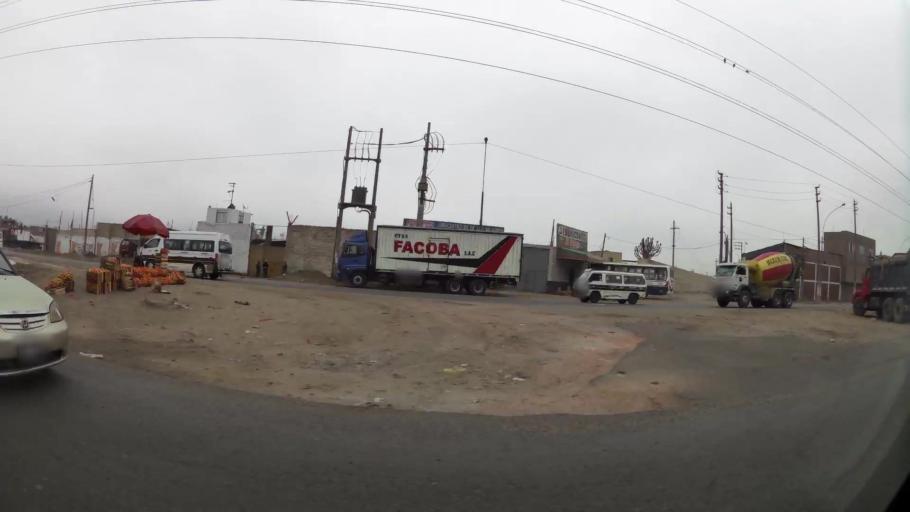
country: PE
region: Lima
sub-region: Lima
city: Urb. Santo Domingo
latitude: -11.9299
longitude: -77.0685
